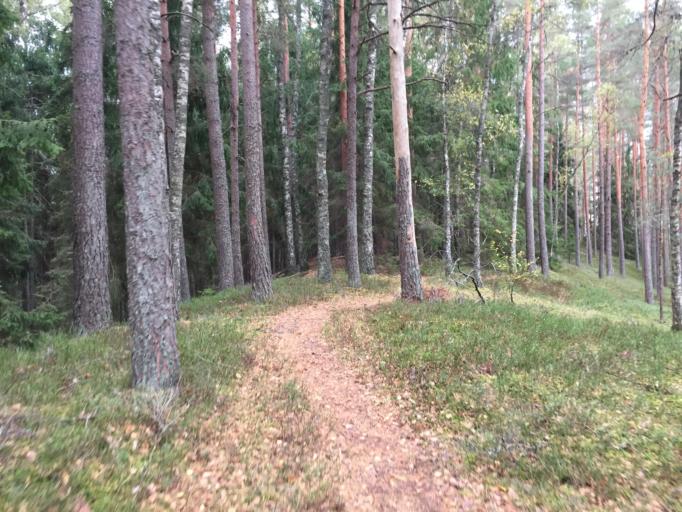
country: LV
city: Tireli
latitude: 56.8912
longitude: 23.5332
